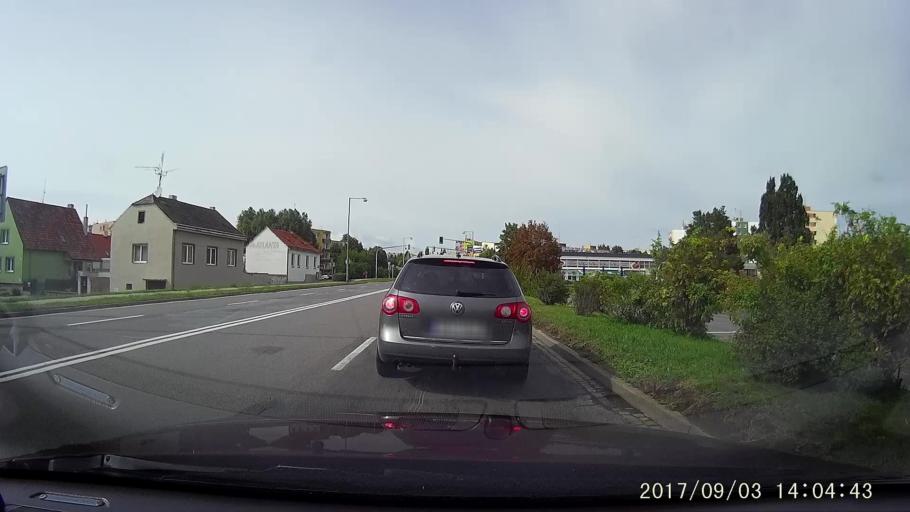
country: CZ
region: South Moravian
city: Dobsice
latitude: 48.8394
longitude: 16.0651
